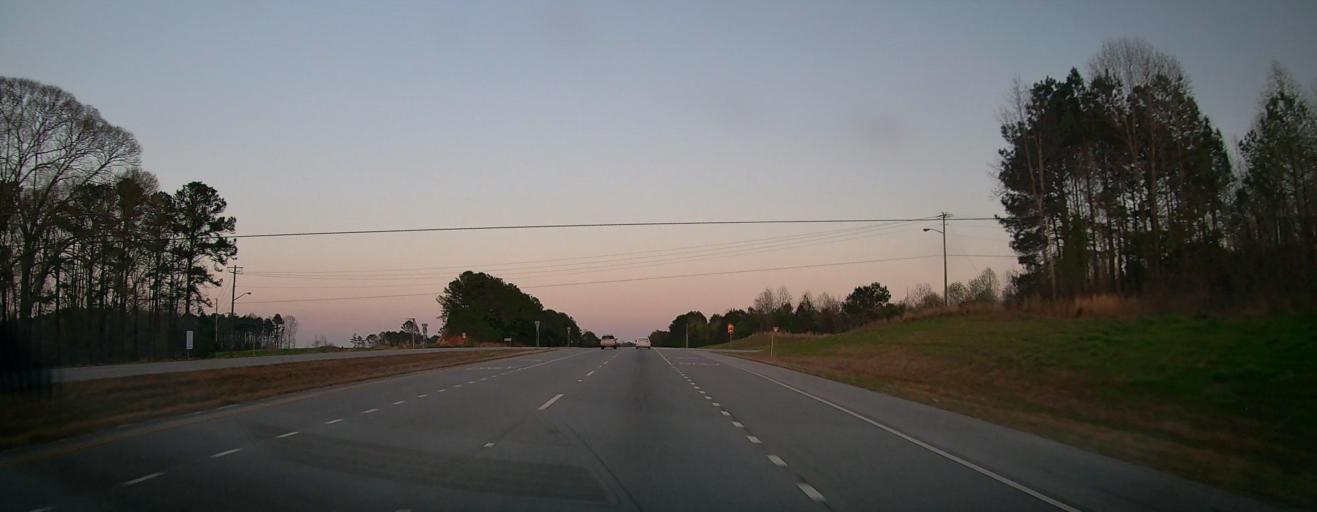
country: US
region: Alabama
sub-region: Tallapoosa County
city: Alexander City
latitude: 32.9064
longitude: -85.9095
